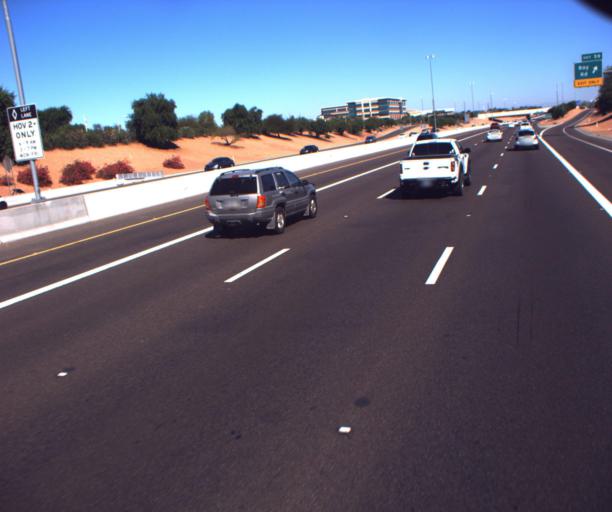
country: US
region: Arizona
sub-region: Maricopa County
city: Chandler
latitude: 33.3143
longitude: -111.8942
